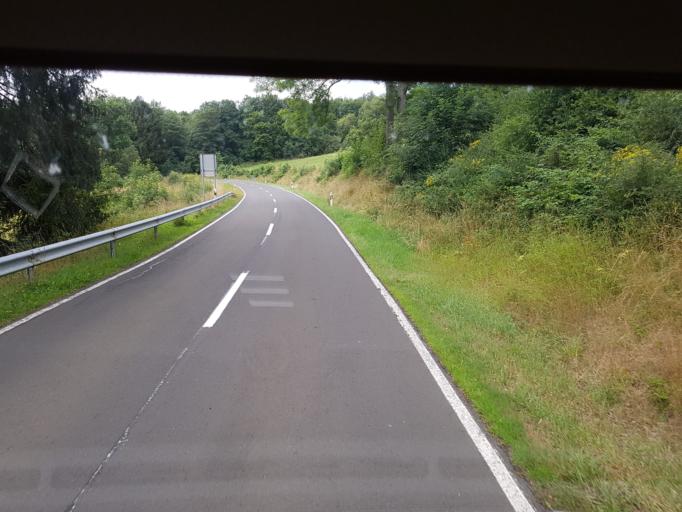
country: DE
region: Rheinland-Pfalz
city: Winterspelt
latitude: 50.2332
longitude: 6.1894
